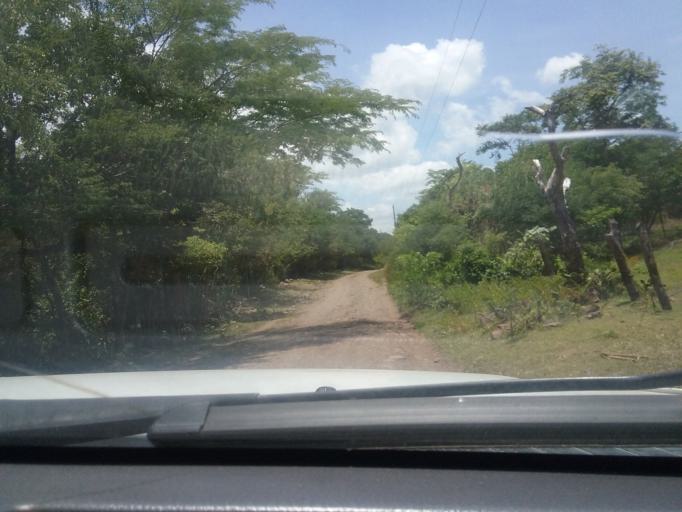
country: NI
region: Matagalpa
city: Terrabona
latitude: 12.6547
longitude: -85.9923
